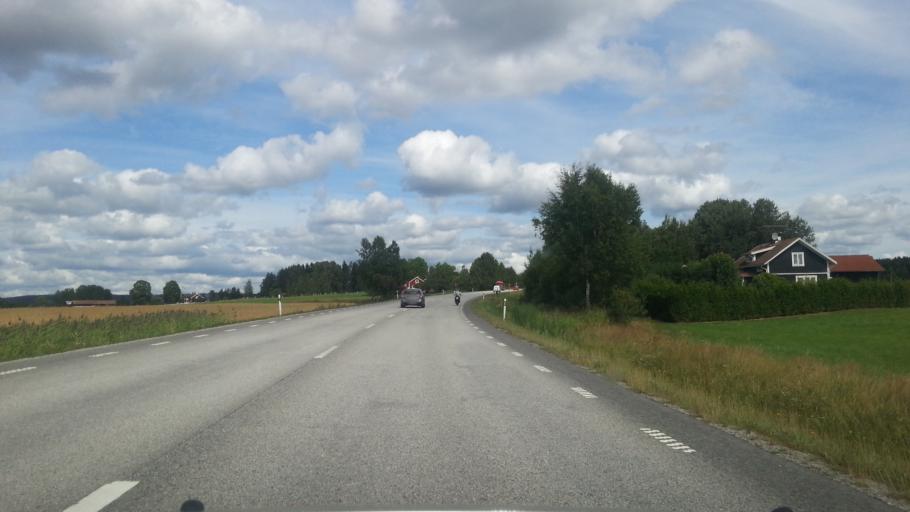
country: SE
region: OErebro
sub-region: Lindesbergs Kommun
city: Lindesberg
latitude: 59.6326
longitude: 15.2162
